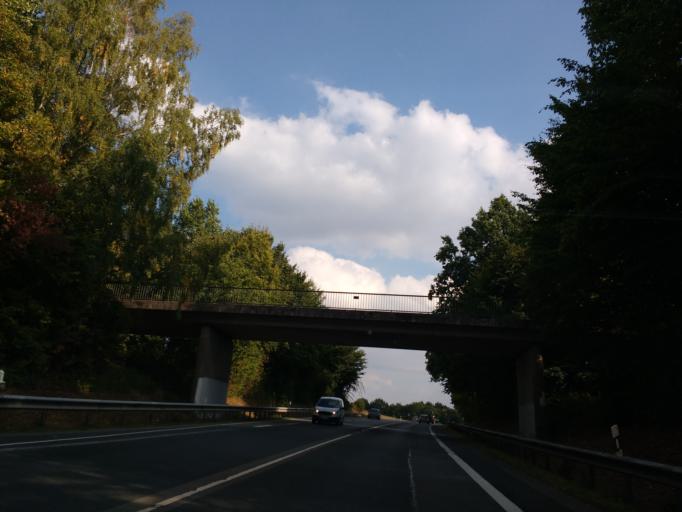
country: DE
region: North Rhine-Westphalia
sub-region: Regierungsbezirk Detmold
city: Blomberg
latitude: 51.9405
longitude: 9.0790
